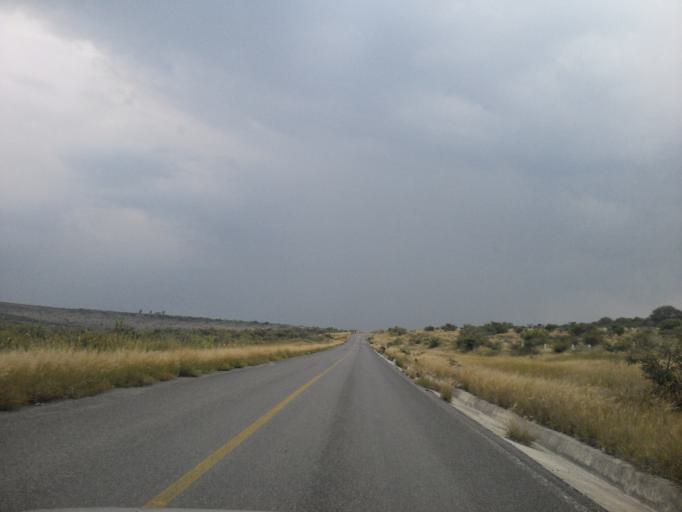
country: MX
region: Jalisco
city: San Diego de Alejandria
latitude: 20.8791
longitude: -102.0703
